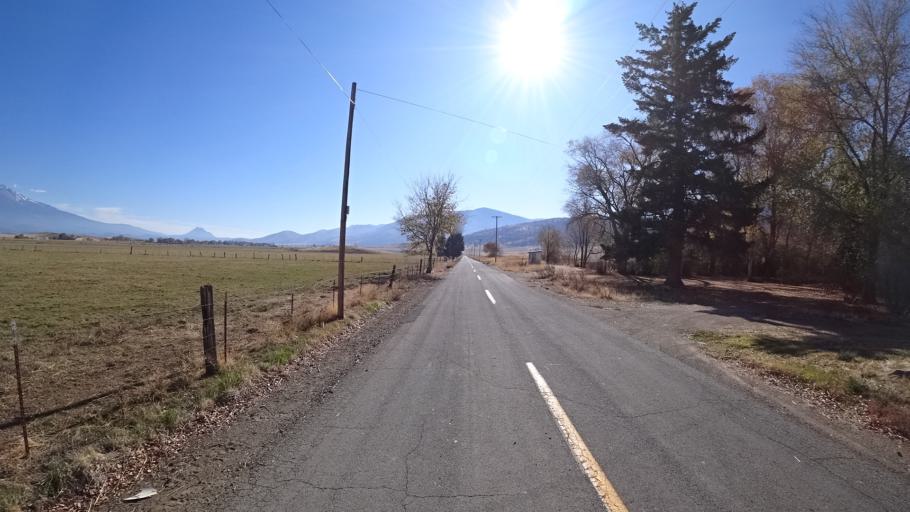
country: US
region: California
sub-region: Siskiyou County
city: Weed
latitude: 41.5347
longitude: -122.5352
